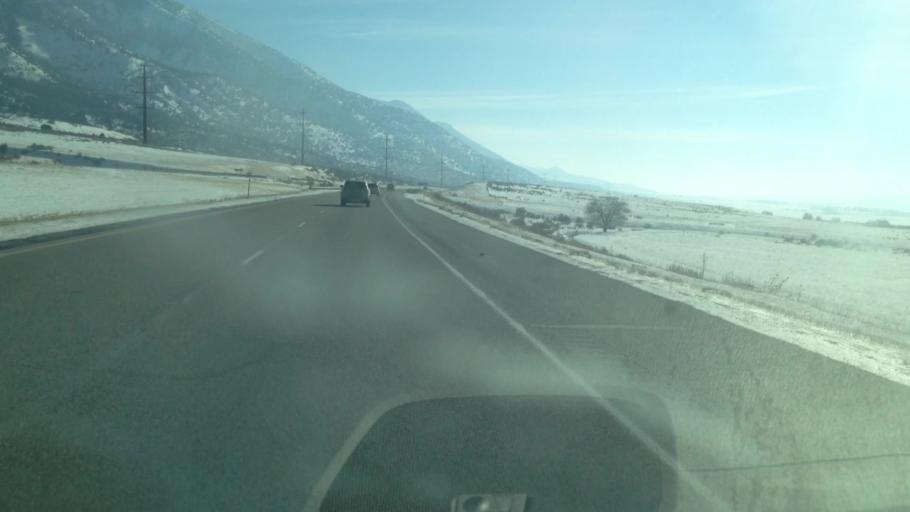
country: US
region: Idaho
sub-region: Oneida County
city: Malad City
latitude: 42.1657
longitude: -112.2226
